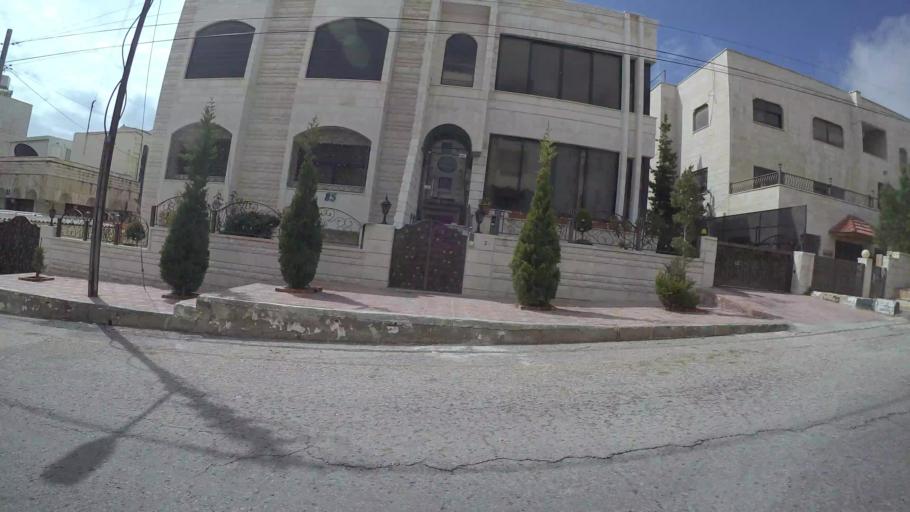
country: JO
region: Amman
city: Al Jubayhah
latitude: 31.9896
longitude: 35.8540
